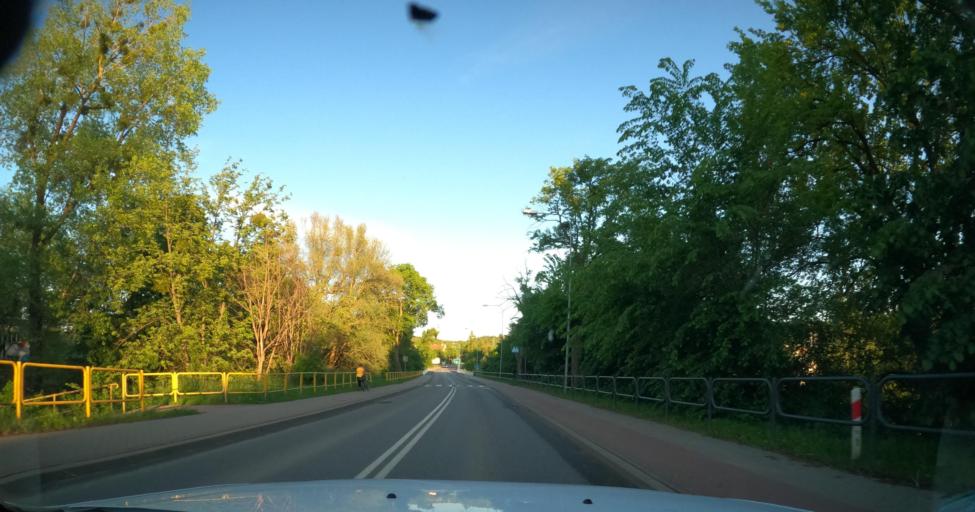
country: PL
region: Warmian-Masurian Voivodeship
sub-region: Powiat lidzbarski
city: Lidzbark Warminski
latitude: 54.1252
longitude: 20.5685
